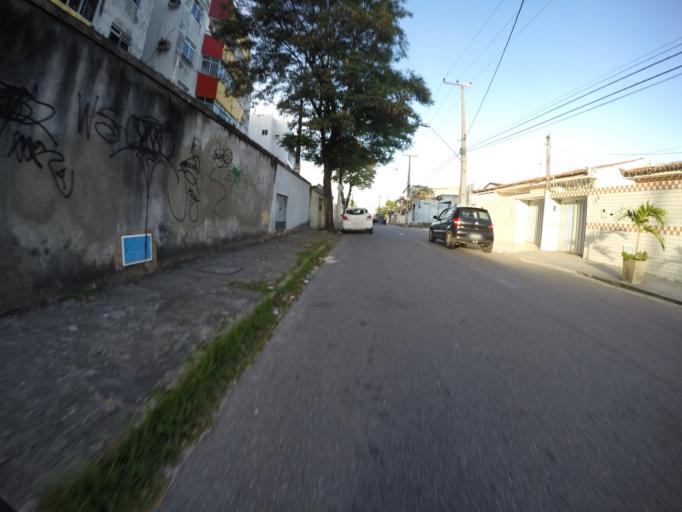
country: BR
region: Ceara
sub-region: Fortaleza
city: Fortaleza
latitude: -3.7571
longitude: -38.5128
